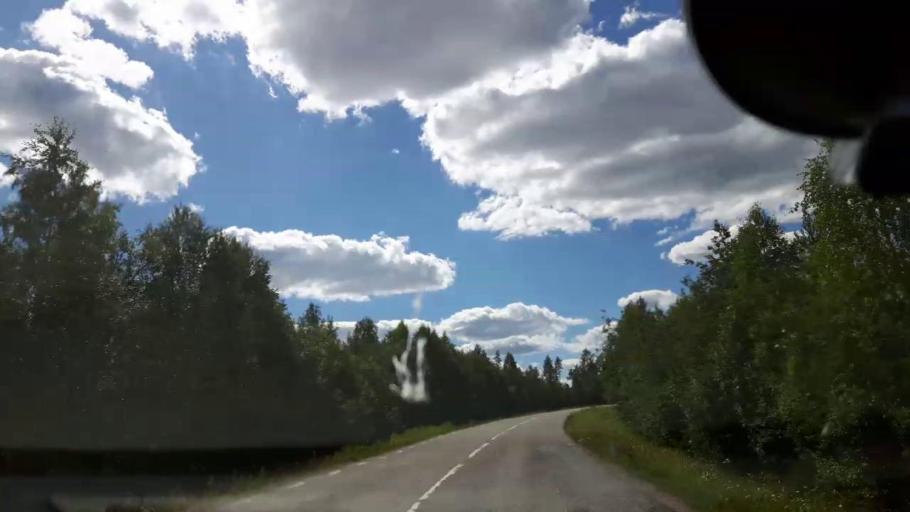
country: SE
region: Jaemtland
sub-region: Ragunda Kommun
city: Hammarstrand
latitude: 63.0369
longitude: 16.3894
